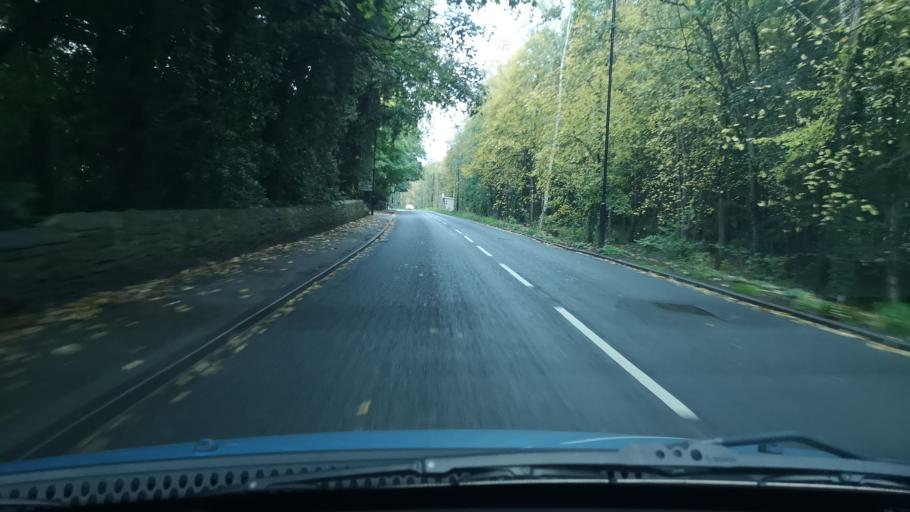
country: GB
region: England
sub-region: Doncaster
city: Campsall
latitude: 53.6200
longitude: -1.1682
